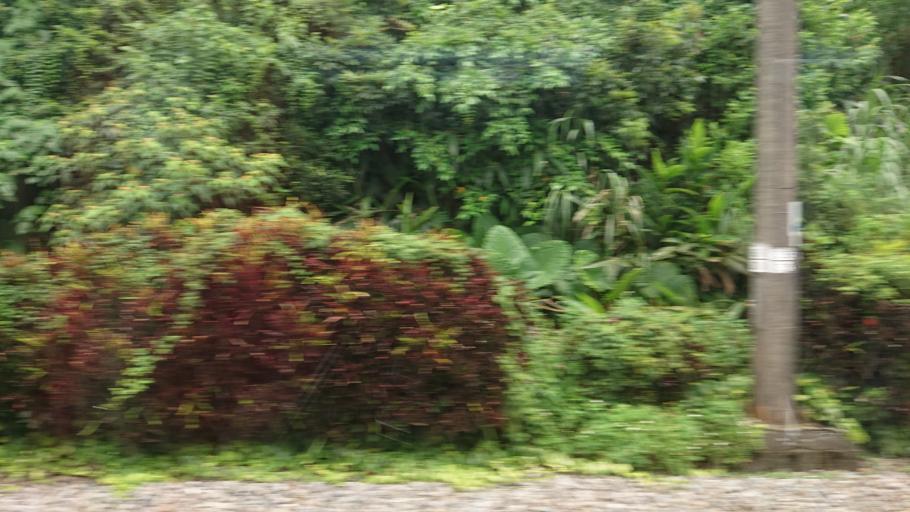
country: TW
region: Taiwan
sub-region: Keelung
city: Keelung
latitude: 24.9804
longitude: 121.9505
